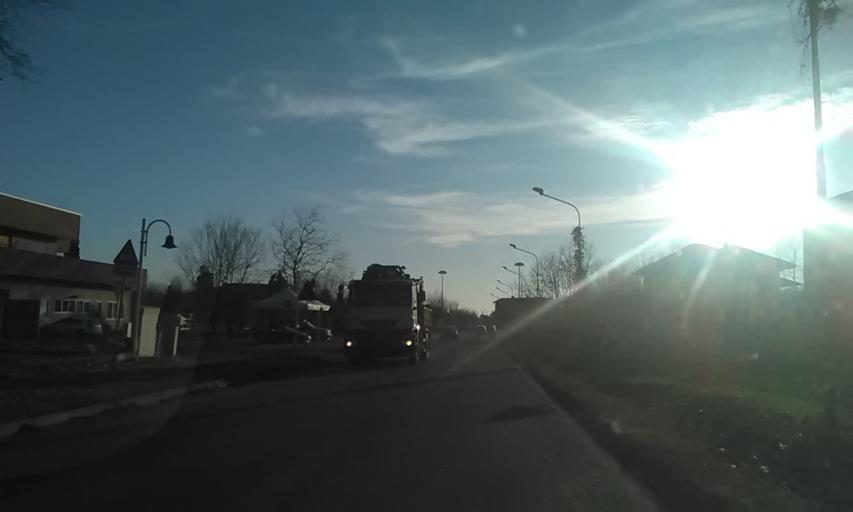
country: IT
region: Piedmont
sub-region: Provincia di Biella
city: Brusnengo
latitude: 45.5650
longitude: 8.2448
